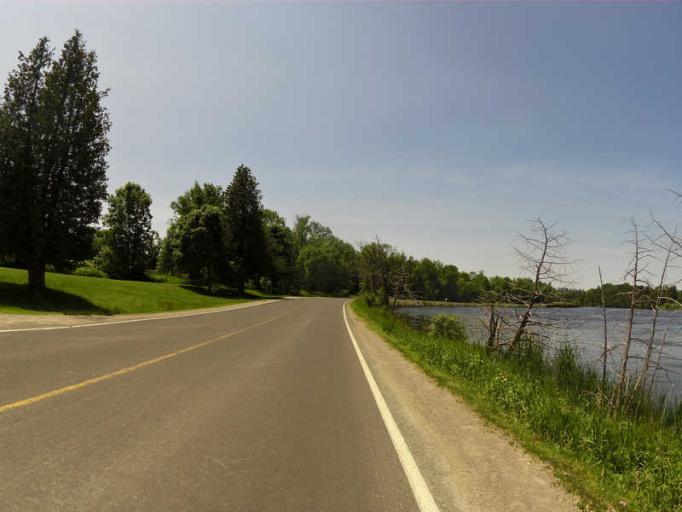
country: CA
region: Ontario
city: Peterborough
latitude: 44.3827
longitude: -78.2723
